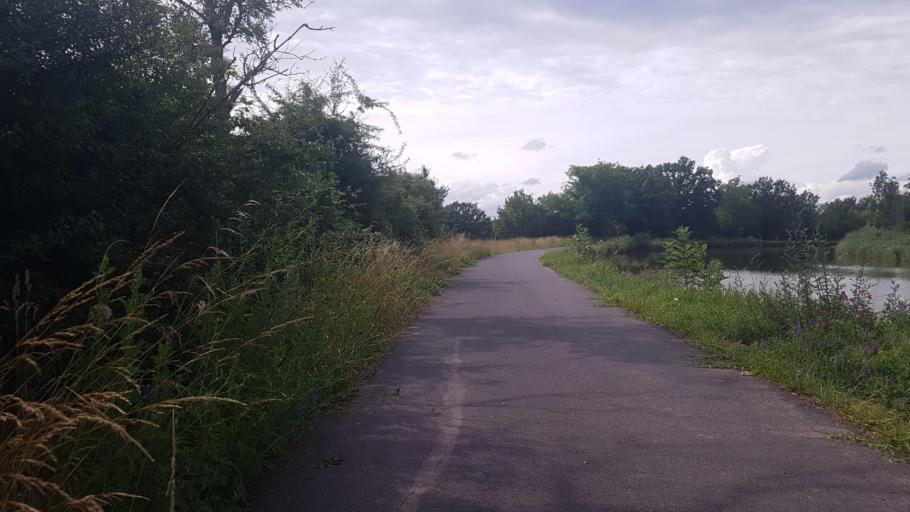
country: FR
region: Lorraine
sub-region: Departement de la Moselle
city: Dieuze
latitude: 48.6916
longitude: 6.7471
